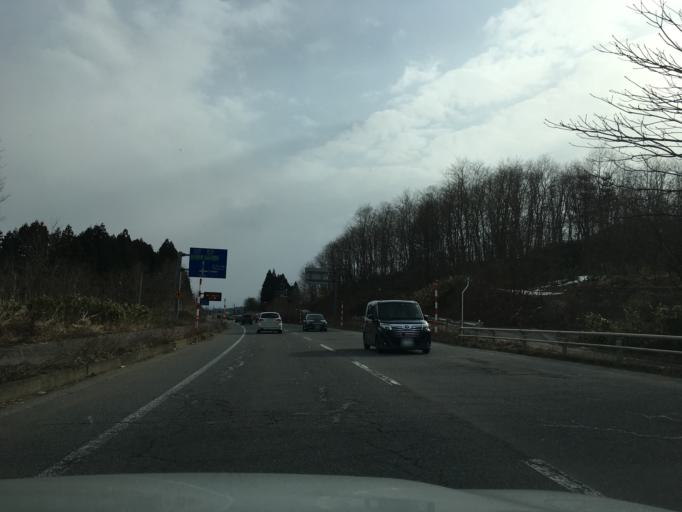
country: JP
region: Aomori
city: Namioka
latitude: 40.7635
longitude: 140.5876
